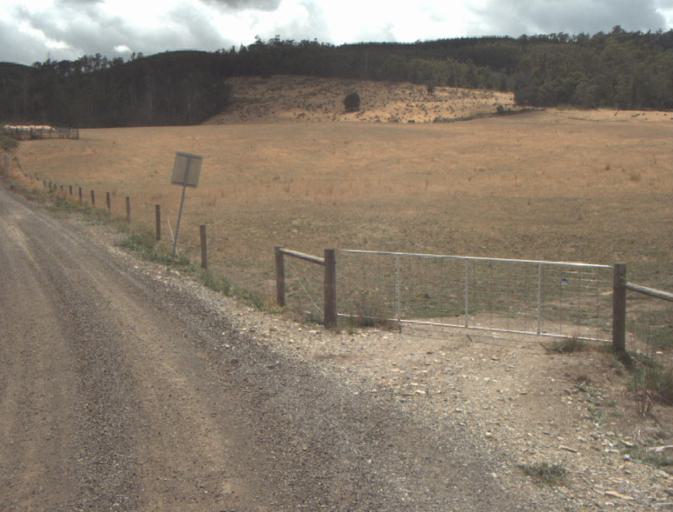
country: AU
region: Tasmania
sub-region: Launceston
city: Mayfield
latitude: -41.2125
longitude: 147.1492
